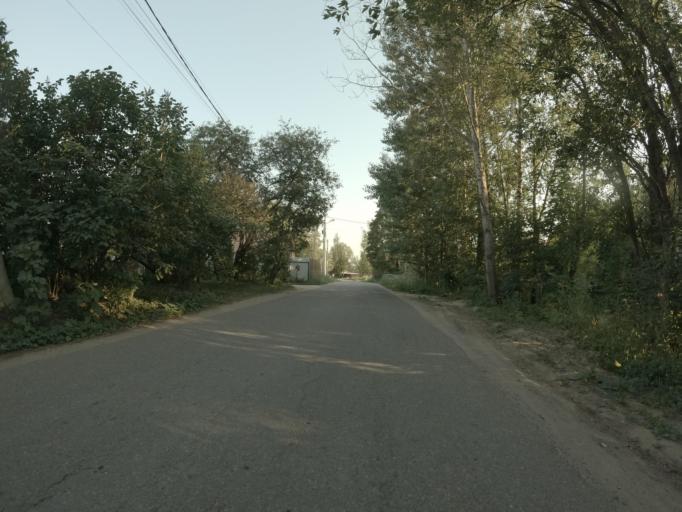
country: RU
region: Leningrad
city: Koltushi
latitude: 59.8934
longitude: 30.6890
